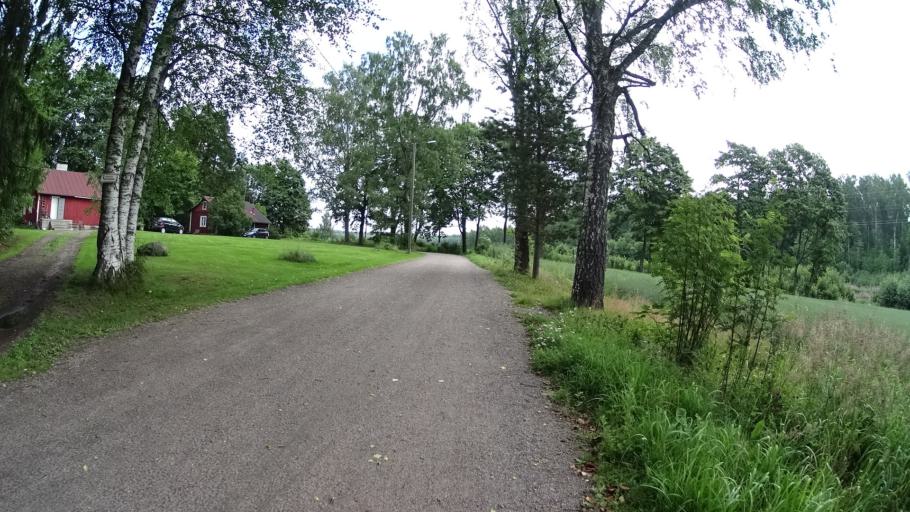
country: FI
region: Uusimaa
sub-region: Helsinki
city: Kilo
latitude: 60.2349
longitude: 24.7871
